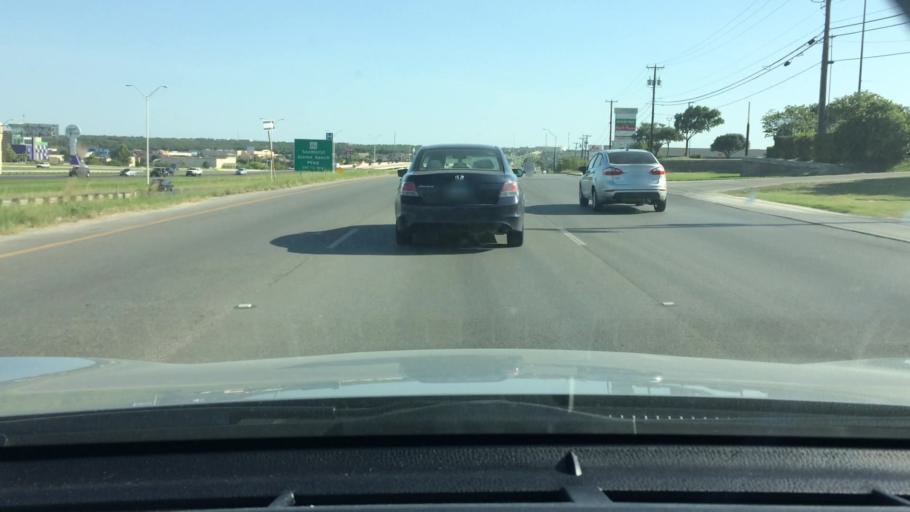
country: US
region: Texas
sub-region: Bexar County
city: Helotes
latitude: 29.4992
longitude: -98.7028
